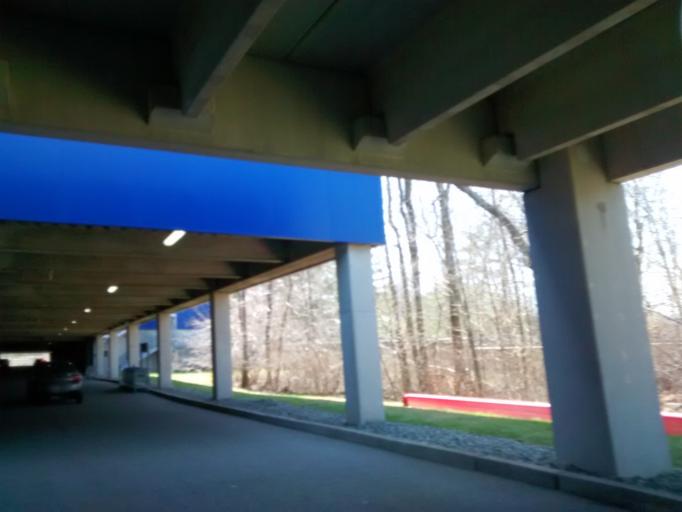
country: US
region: Massachusetts
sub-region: Norfolk County
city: Avon
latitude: 42.1390
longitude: -71.0679
